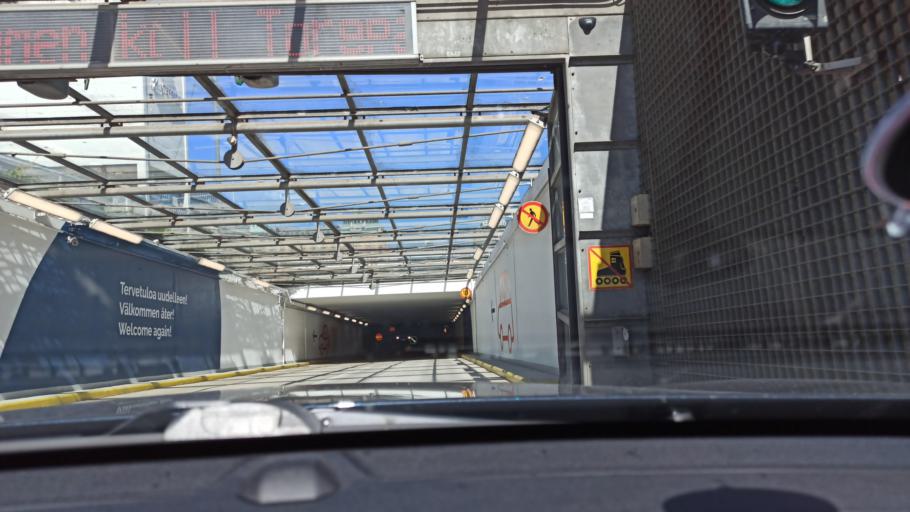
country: FI
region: Ostrobothnia
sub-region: Vaasa
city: Vaasa
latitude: 63.0945
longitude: 21.6171
